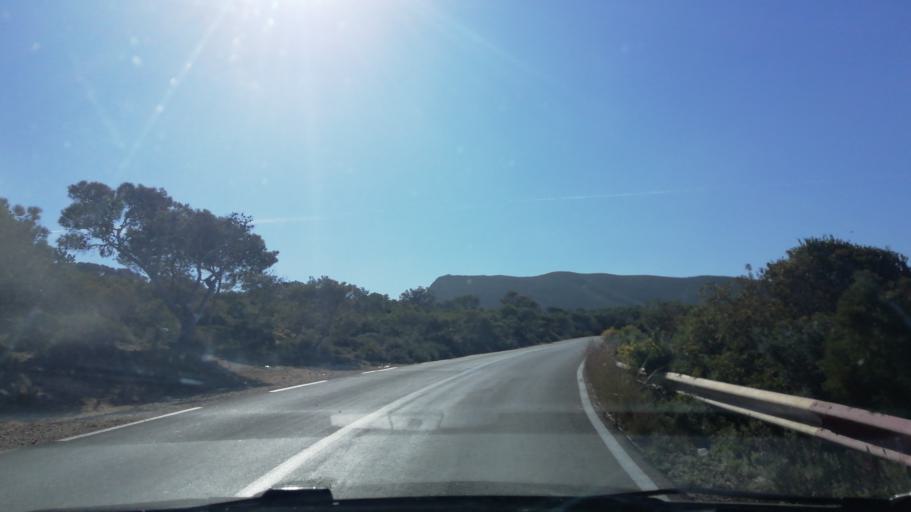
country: DZ
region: Ain Temouchent
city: El Amria
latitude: 35.6447
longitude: -1.0535
